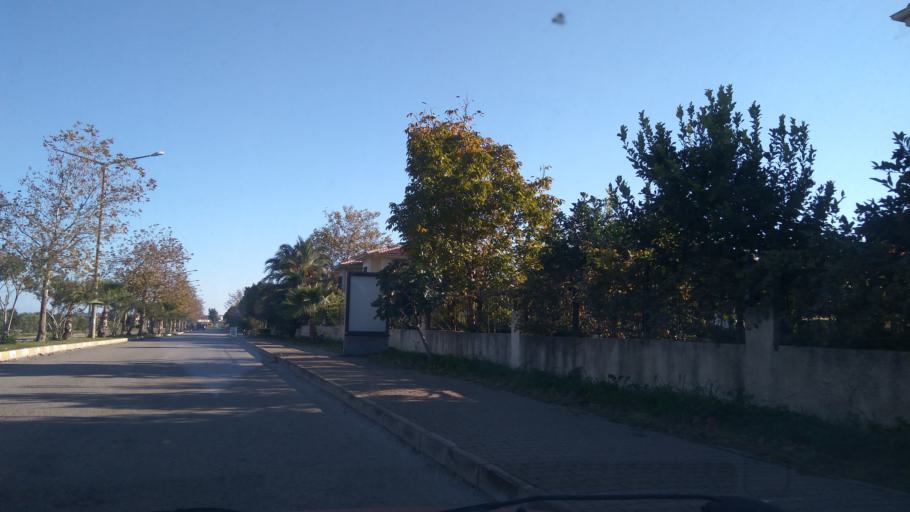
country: TR
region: Antalya
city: Kemer
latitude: 36.5698
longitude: 30.5591
